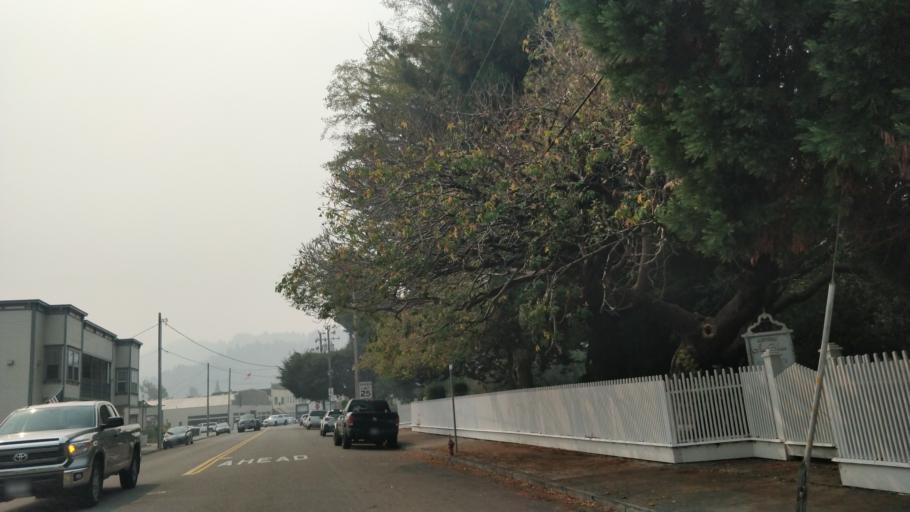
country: US
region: California
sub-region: Humboldt County
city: Ferndale
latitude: 40.5790
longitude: -124.2615
